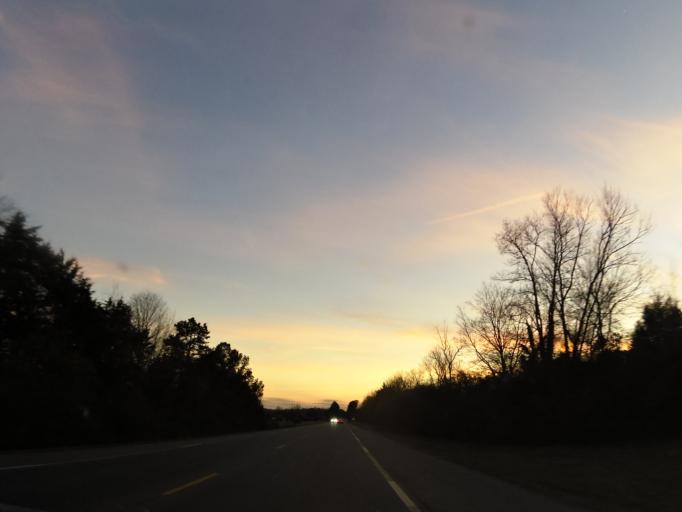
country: US
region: Tennessee
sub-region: Bradley County
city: Wildwood Lake
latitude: 35.0465
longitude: -84.9026
